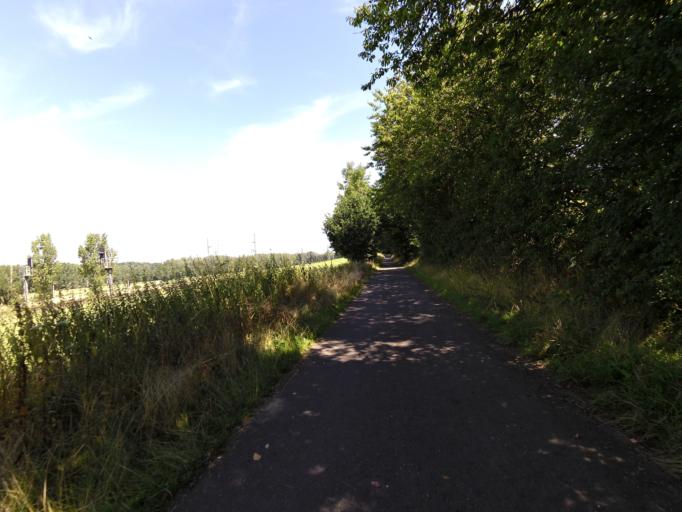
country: DE
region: North Rhine-Westphalia
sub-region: Regierungsbezirk Koln
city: Herzogenrath
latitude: 50.9057
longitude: 6.0841
